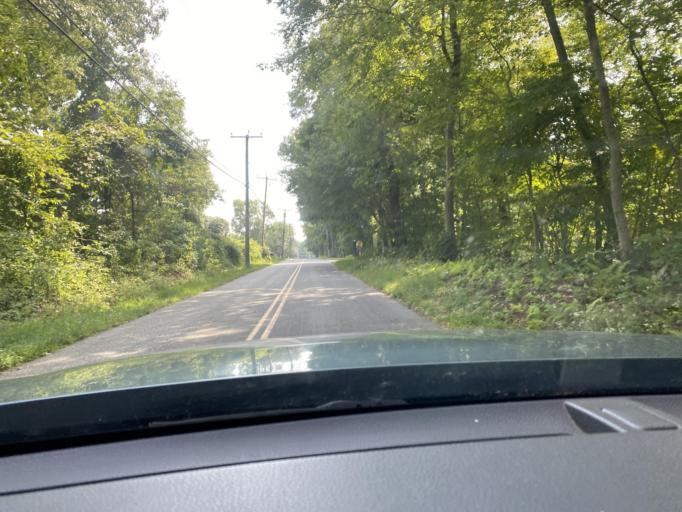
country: US
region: Connecticut
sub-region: New London County
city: Colchester
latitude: 41.6387
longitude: -72.2932
